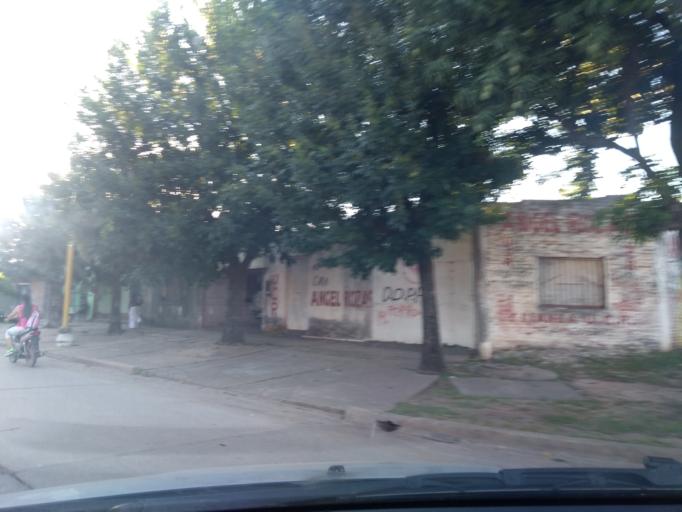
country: AR
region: Chaco
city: Barranqueras
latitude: -27.4815
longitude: -58.9380
